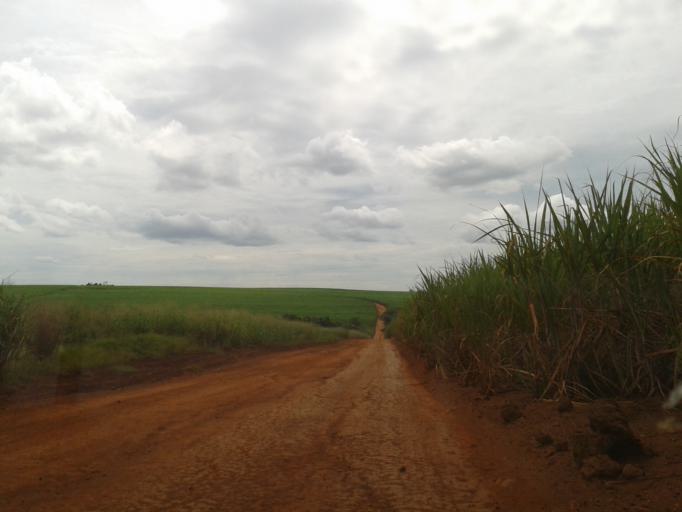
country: BR
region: Minas Gerais
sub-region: Centralina
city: Centralina
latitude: -18.7770
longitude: -49.2579
